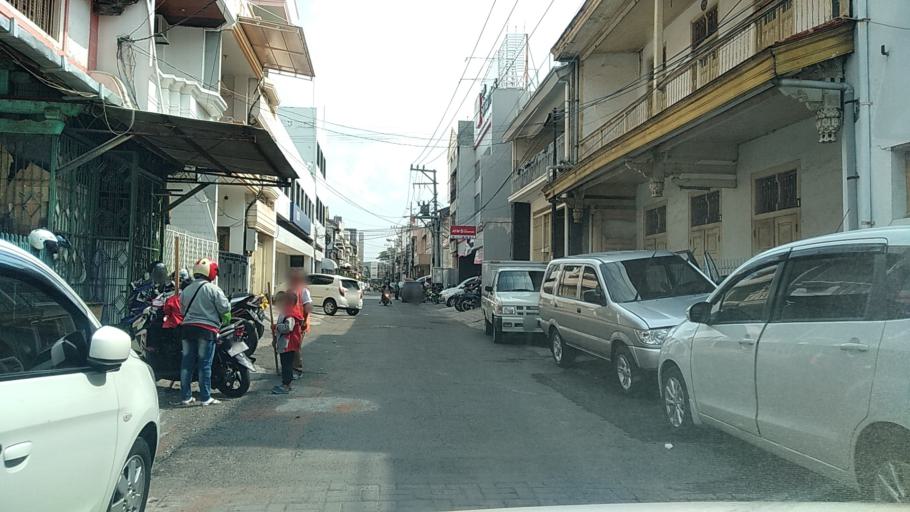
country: ID
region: Central Java
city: Semarang
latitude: -6.9748
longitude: 110.4272
